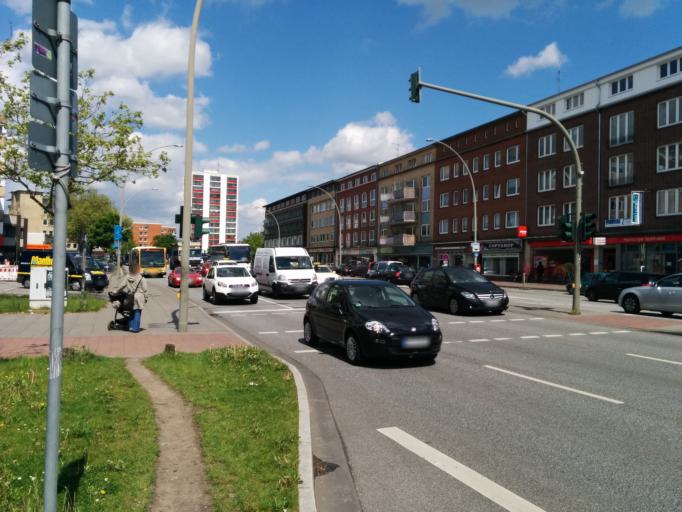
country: DE
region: Hamburg
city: Hamburg
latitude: 53.5784
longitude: 10.0392
